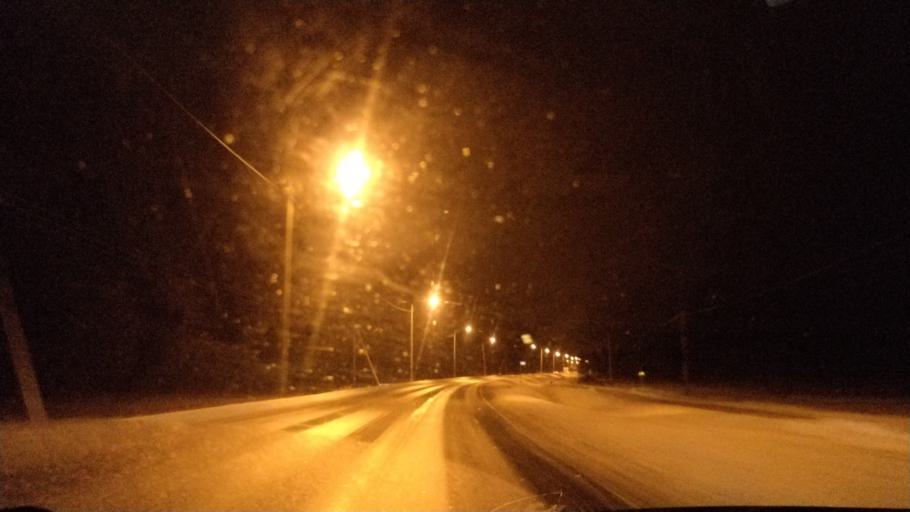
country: FI
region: Lapland
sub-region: Rovaniemi
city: Rovaniemi
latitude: 66.3107
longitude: 25.3616
